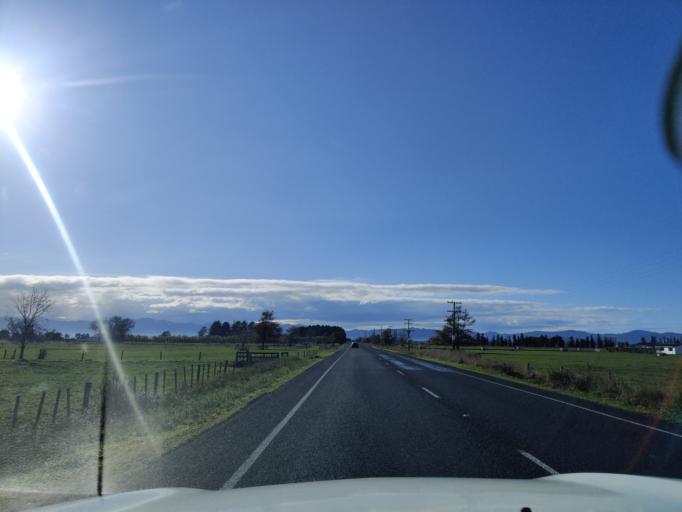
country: NZ
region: Waikato
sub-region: Hauraki District
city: Ngatea
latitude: -37.2738
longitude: 175.5121
